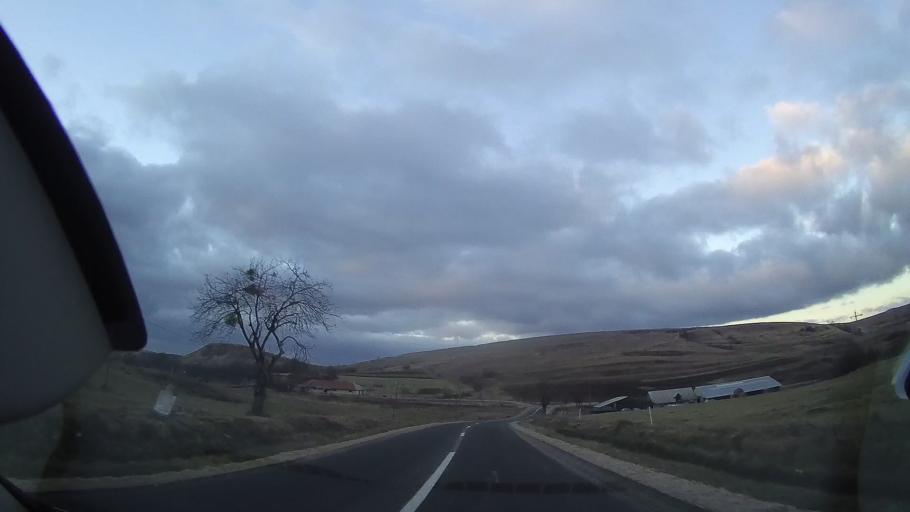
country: RO
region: Cluj
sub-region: Comuna Izvoru Crisului
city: Izvoru Crisului
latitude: 46.8020
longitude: 23.1101
